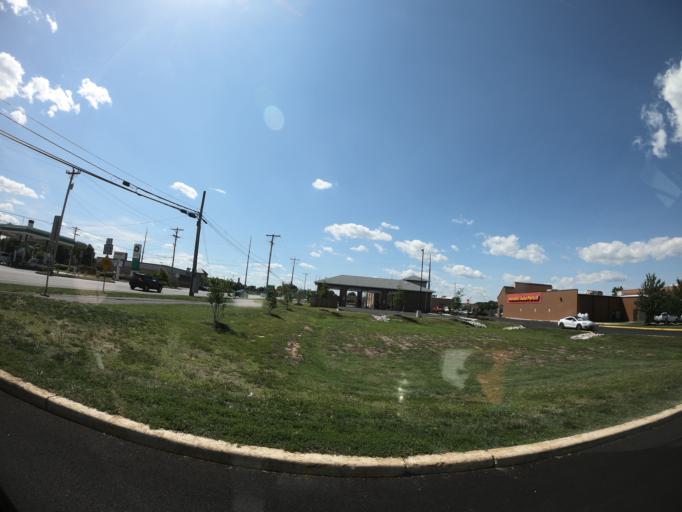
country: US
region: Delaware
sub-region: Sussex County
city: Milford
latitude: 38.9150
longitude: -75.4407
